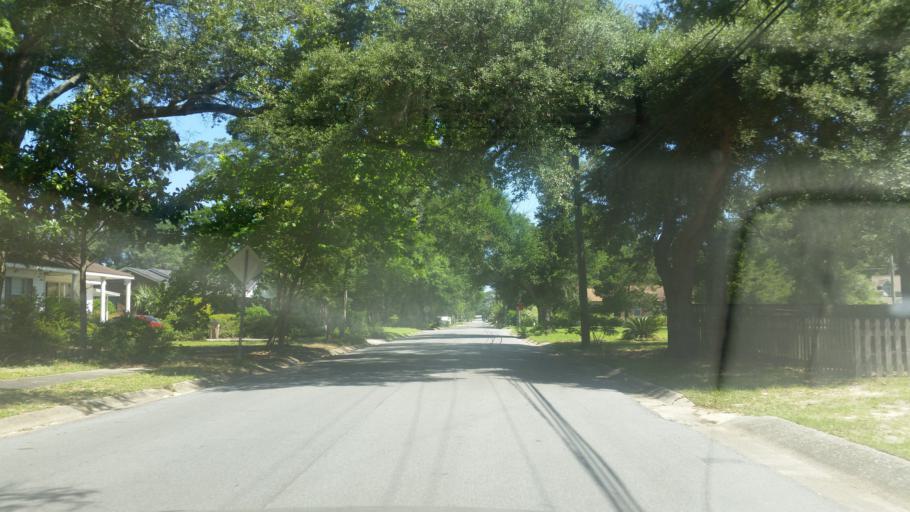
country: US
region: Florida
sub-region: Escambia County
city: Pensacola
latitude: 30.4305
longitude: -87.2223
